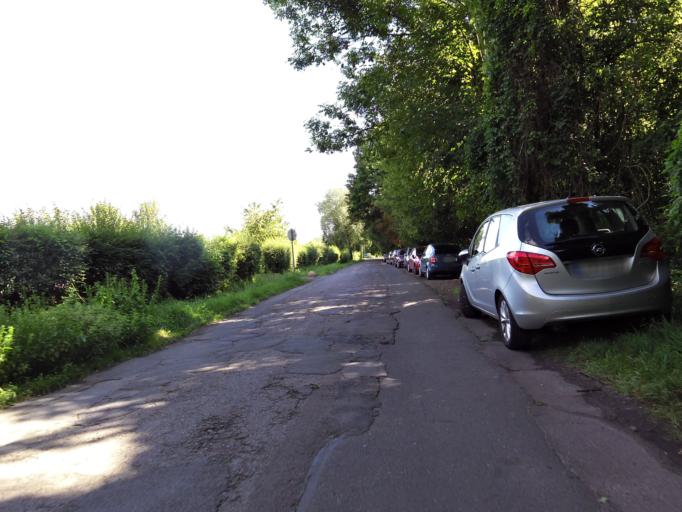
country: DE
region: Saxony
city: Markkleeberg
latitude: 51.2912
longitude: 12.4021
